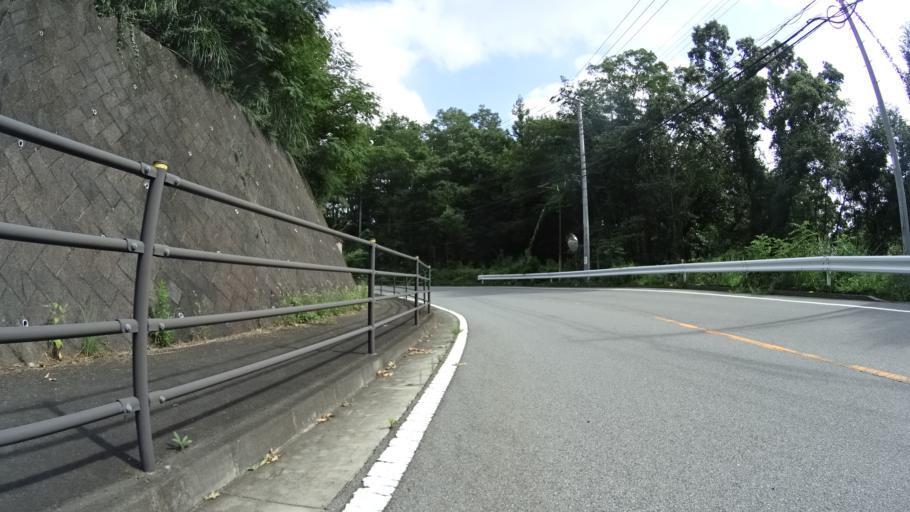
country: JP
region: Yamanashi
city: Kofu-shi
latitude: 35.7070
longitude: 138.5545
